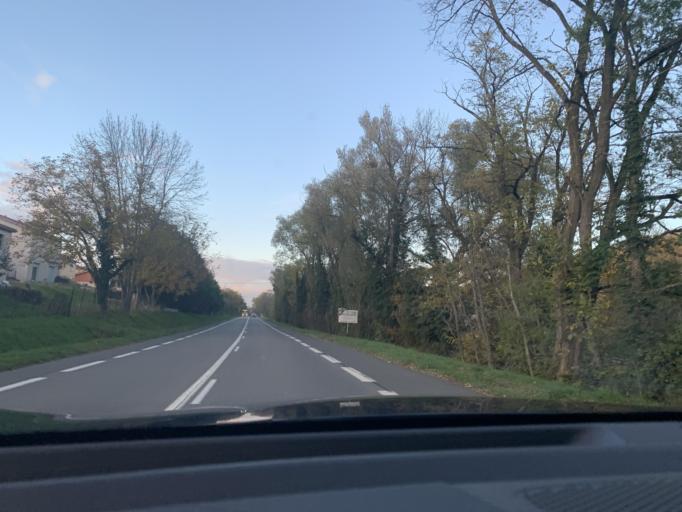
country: FR
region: Rhone-Alpes
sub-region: Departement du Rhone
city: Liergues
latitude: 45.9576
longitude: 4.6674
